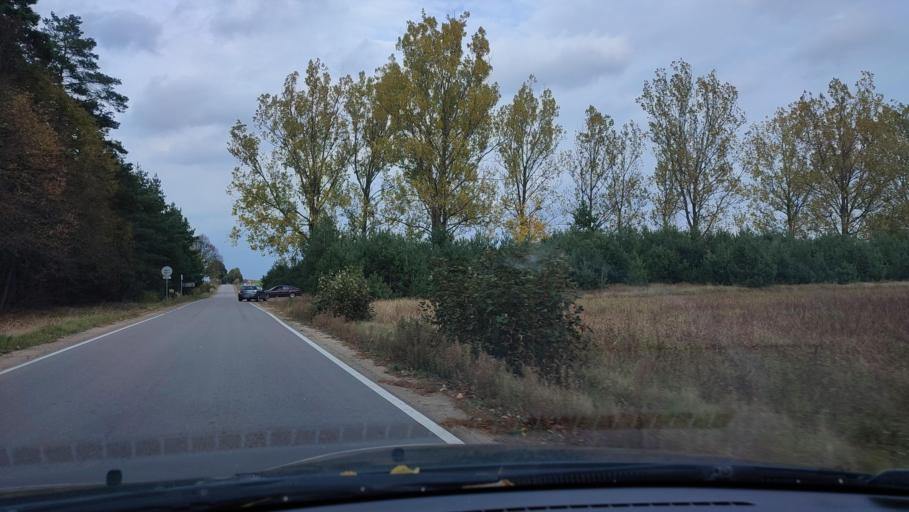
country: PL
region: Masovian Voivodeship
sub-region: Powiat mlawski
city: Mlawa
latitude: 53.1849
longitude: 20.3775
